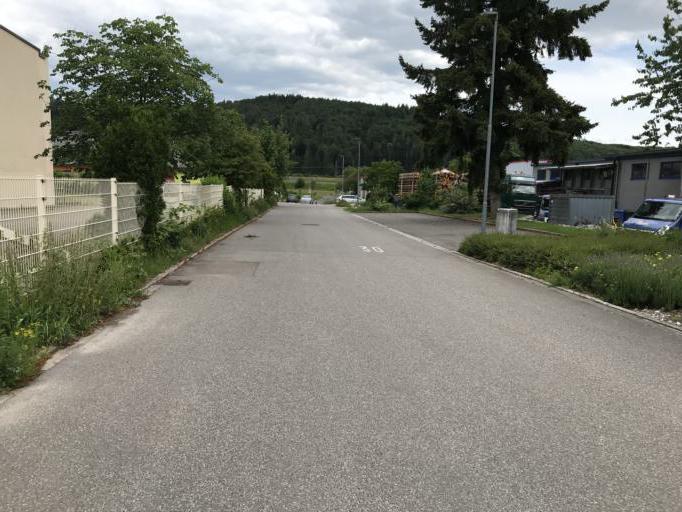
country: DE
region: Baden-Wuerttemberg
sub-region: Freiburg Region
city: Hausen
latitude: 47.6758
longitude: 7.8397
